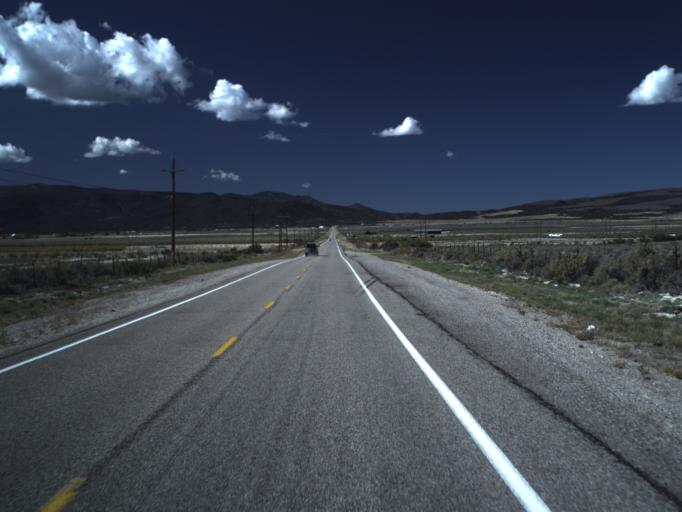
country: US
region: Utah
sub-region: Iron County
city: Cedar City
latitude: 37.6649
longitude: -113.2036
